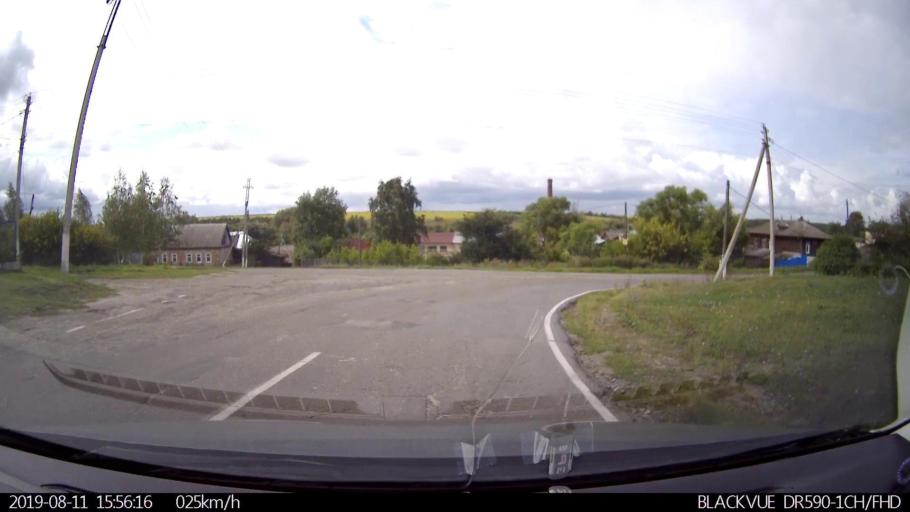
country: RU
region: Ulyanovsk
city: Ignatovka
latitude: 53.9481
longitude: 47.6496
